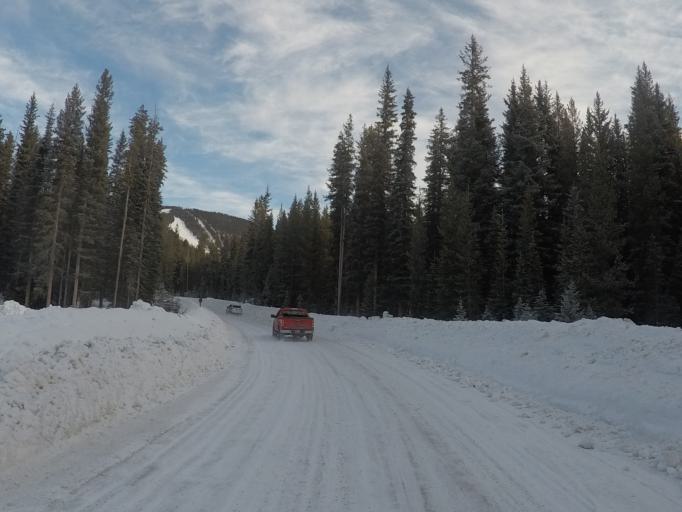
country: US
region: Montana
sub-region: Granite County
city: Philipsburg
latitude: 46.2416
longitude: -113.2433
